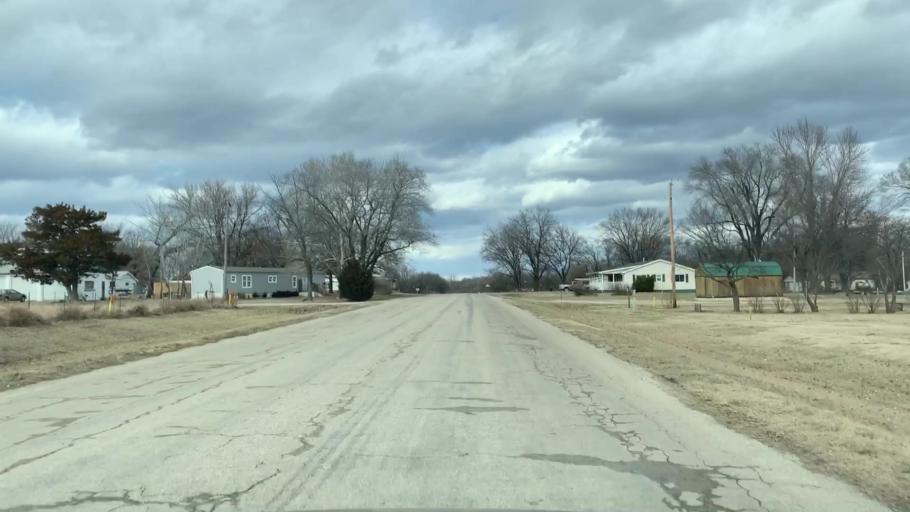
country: US
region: Kansas
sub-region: Neosho County
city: Chanute
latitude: 37.7441
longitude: -95.4705
